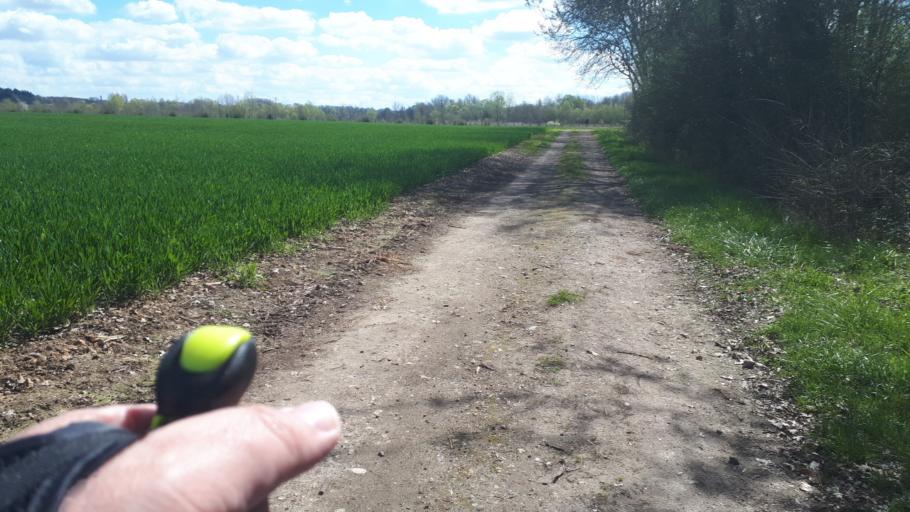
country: FR
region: Centre
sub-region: Departement du Loir-et-Cher
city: Villiers-sur-Loir
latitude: 47.7916
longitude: 0.9913
